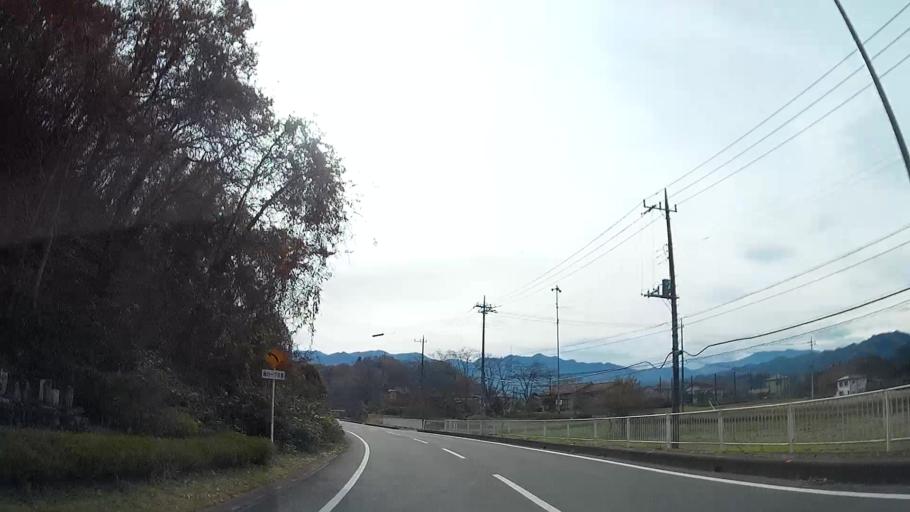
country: JP
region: Saitama
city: Chichibu
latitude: 36.0037
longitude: 139.0386
